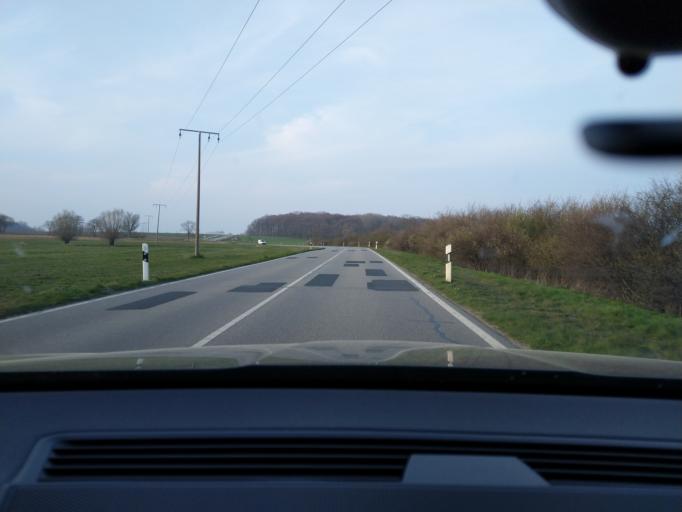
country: DE
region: Mecklenburg-Vorpommern
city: Kramerhof
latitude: 54.3349
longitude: 13.0296
